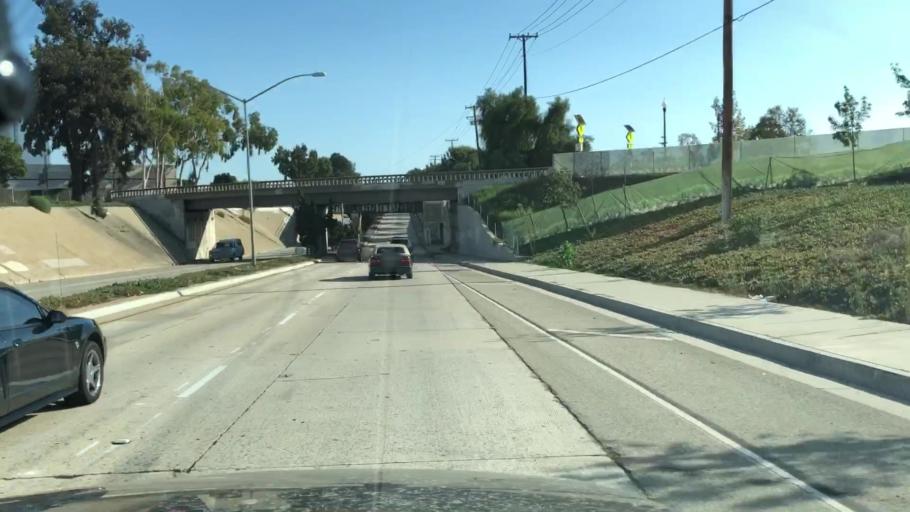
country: US
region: California
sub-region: Ventura County
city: El Rio
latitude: 34.2342
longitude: -119.1799
